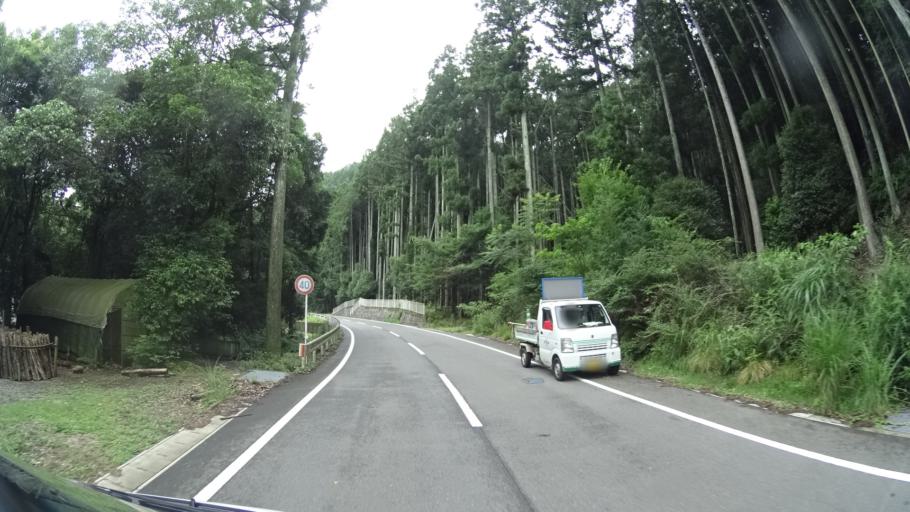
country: JP
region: Kyoto
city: Kameoka
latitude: 35.0593
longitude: 135.4280
